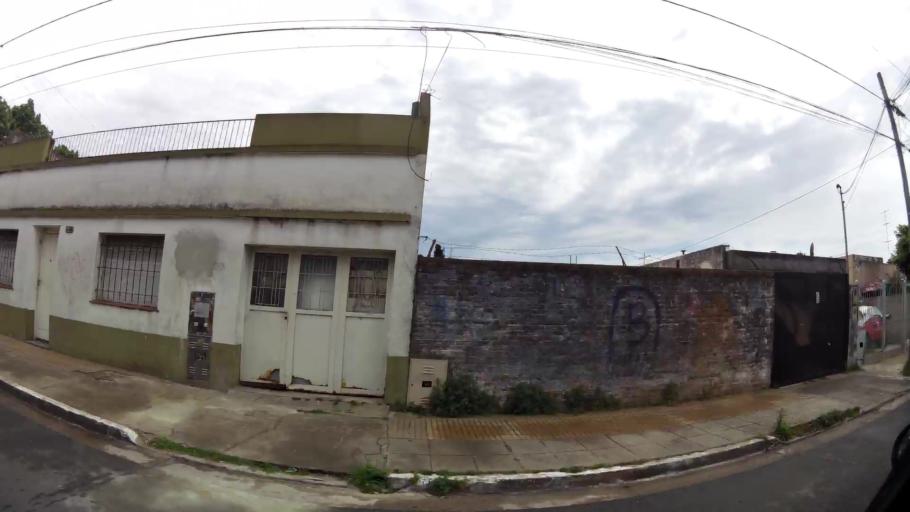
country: AR
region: Buenos Aires
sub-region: Partido de Quilmes
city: Quilmes
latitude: -34.7579
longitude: -58.2047
